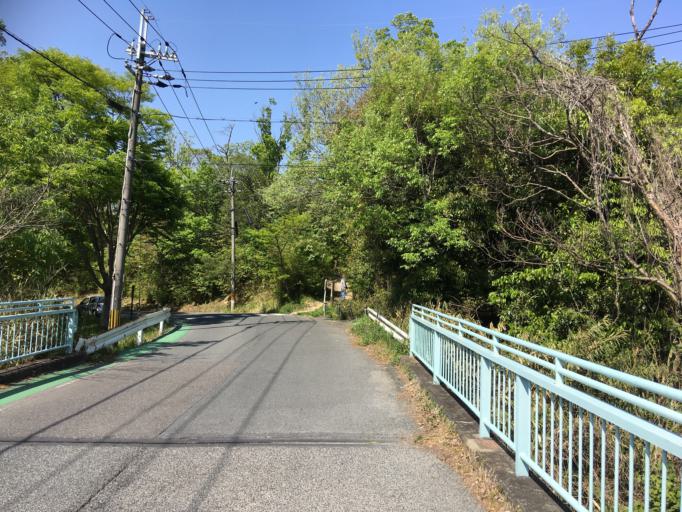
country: JP
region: Nara
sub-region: Ikoma-shi
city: Ikoma
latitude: 34.6948
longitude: 135.7171
